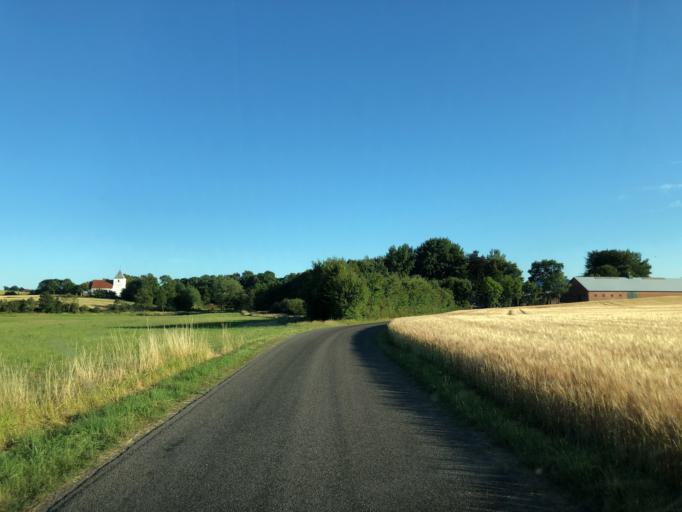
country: DK
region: Central Jutland
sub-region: Horsens Kommune
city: Horsens
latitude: 55.9338
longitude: 9.8669
